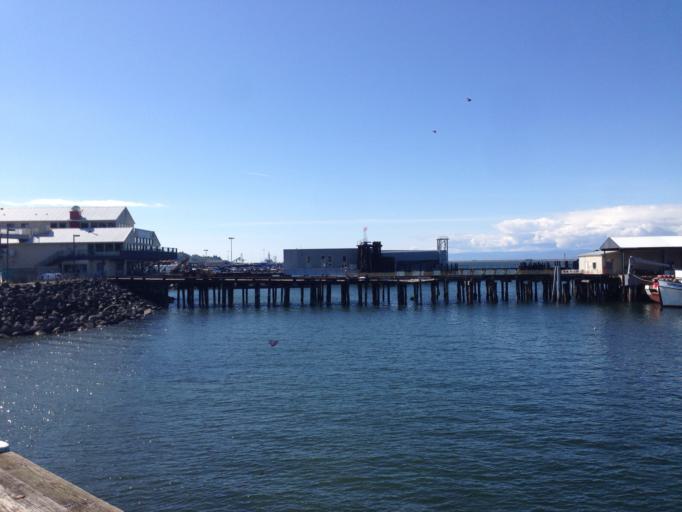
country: US
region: Washington
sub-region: Clallam County
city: Port Angeles
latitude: 48.1208
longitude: -123.4286
